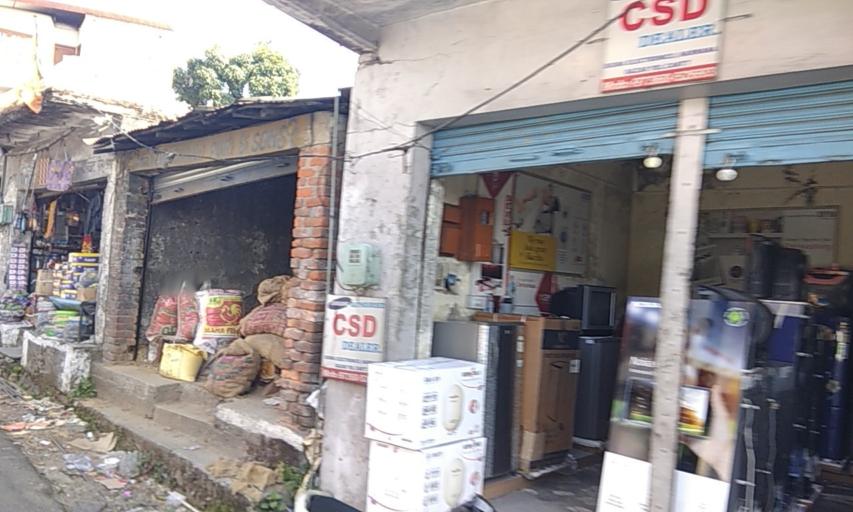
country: IN
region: Himachal Pradesh
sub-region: Kangra
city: Dharmsala
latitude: 32.1719
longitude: 76.3875
